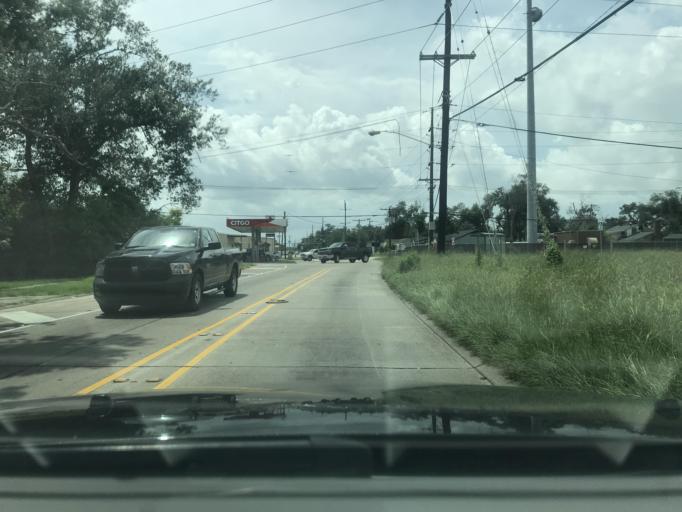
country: US
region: Louisiana
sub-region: Calcasieu Parish
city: Lake Charles
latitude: 30.2131
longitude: -93.2009
